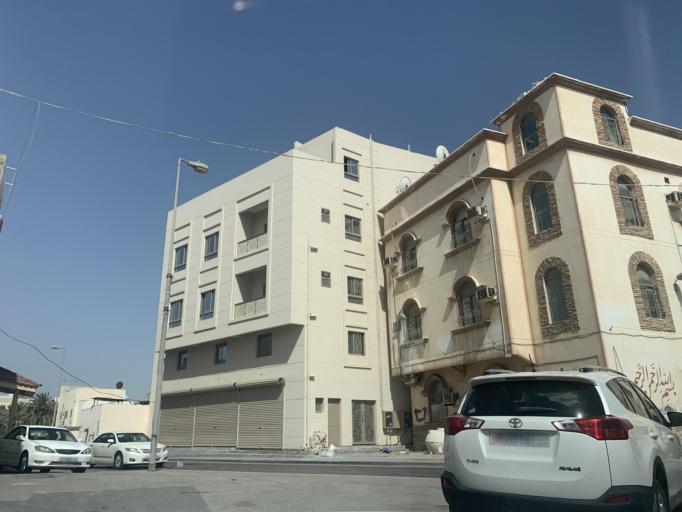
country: BH
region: Manama
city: Jidd Hafs
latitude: 26.2068
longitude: 50.5555
